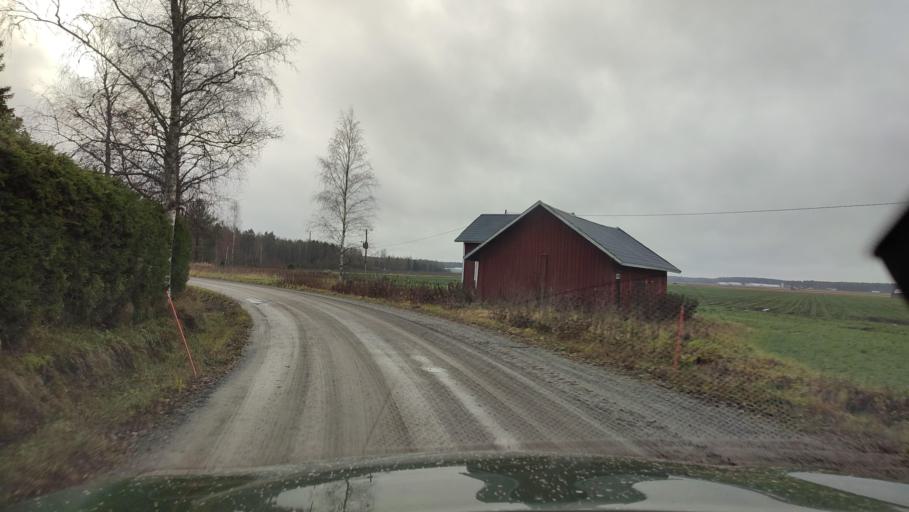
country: FI
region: Ostrobothnia
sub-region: Sydosterbotten
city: Naerpes
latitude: 62.4515
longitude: 21.4570
